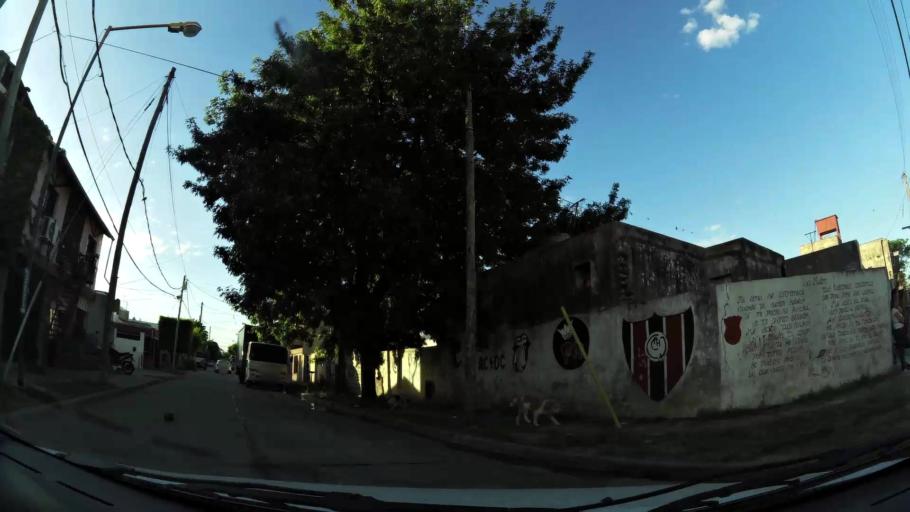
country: AR
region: Buenos Aires
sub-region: Partido de General San Martin
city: General San Martin
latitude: -34.5666
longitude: -58.5284
